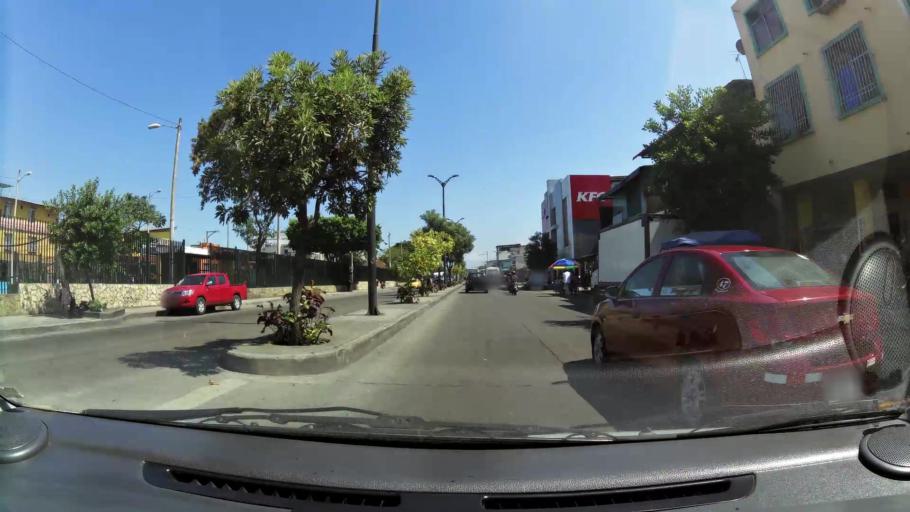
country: EC
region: Guayas
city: Guayaquil
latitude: -2.2096
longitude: -79.9293
